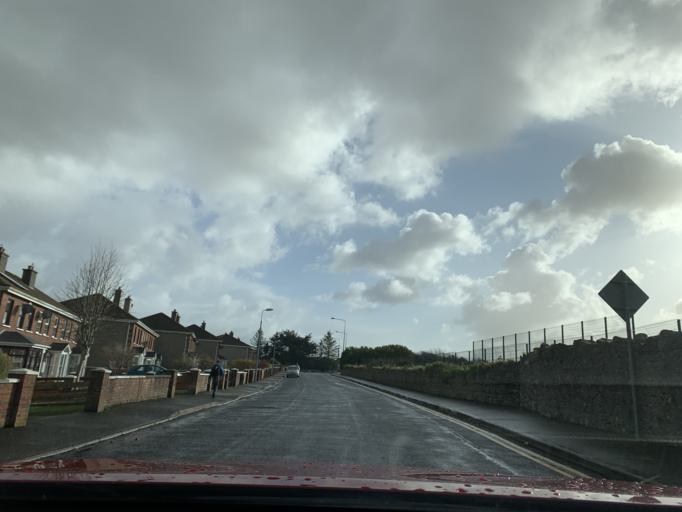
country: IE
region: Connaught
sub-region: Sligo
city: Sligo
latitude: 54.2654
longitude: -8.4768
